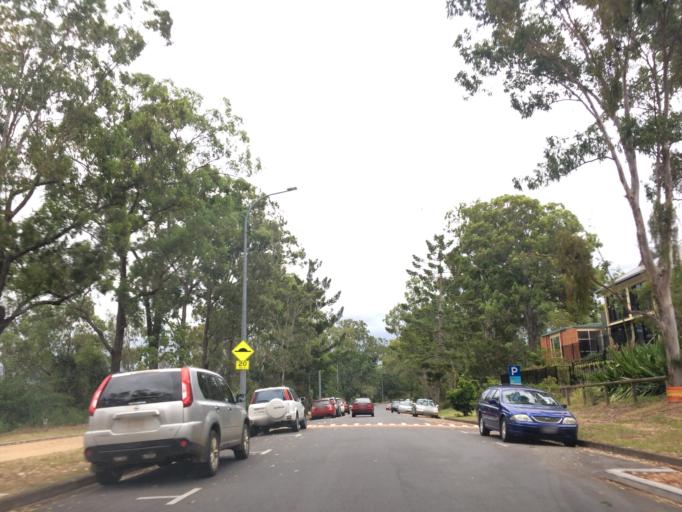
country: AU
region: Queensland
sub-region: Brisbane
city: Yeronga
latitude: -27.5024
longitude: 153.0148
